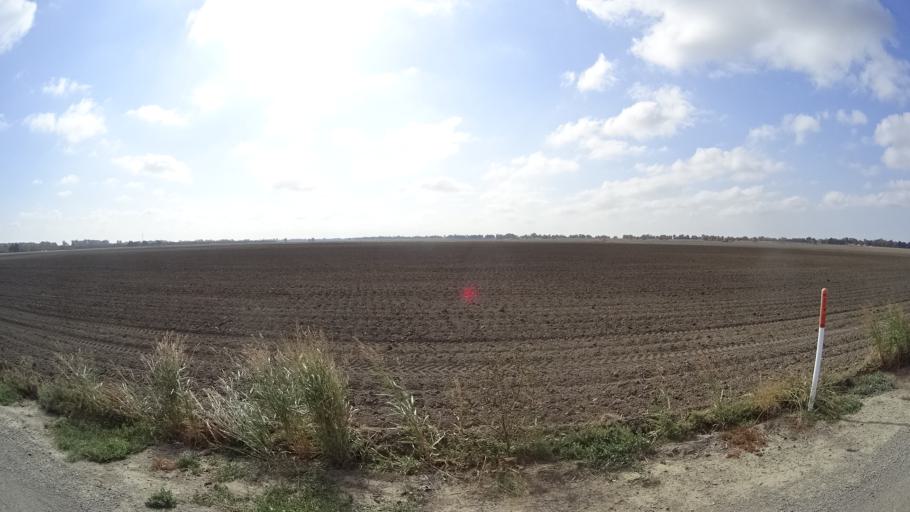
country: US
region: California
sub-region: Yolo County
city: Woodland
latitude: 38.7958
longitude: -121.7079
